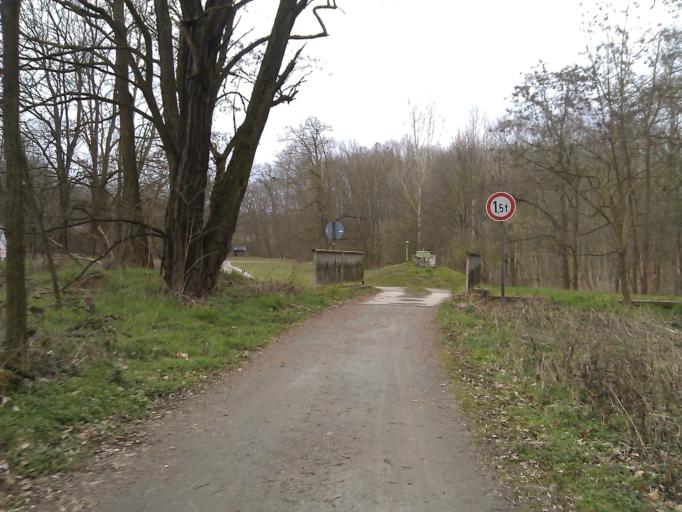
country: DE
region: Hesse
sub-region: Regierungsbezirk Darmstadt
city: Trebur
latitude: 49.9605
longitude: 8.4171
